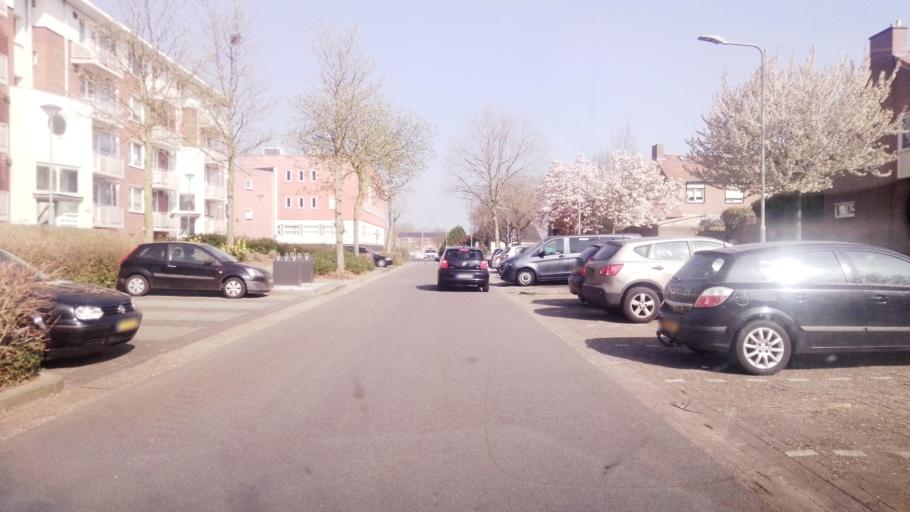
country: NL
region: Limburg
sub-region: Gemeente Venlo
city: Tegelen
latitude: 51.3354
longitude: 6.1318
